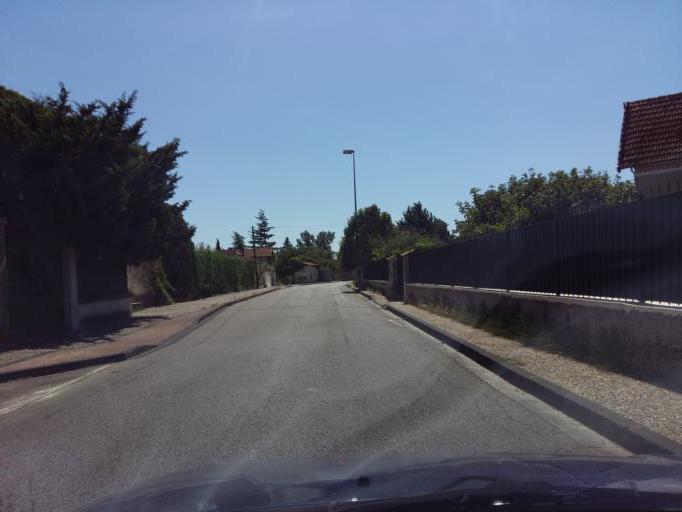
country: FR
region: Provence-Alpes-Cote d'Azur
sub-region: Departement du Vaucluse
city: Sarrians
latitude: 44.0856
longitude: 4.9797
